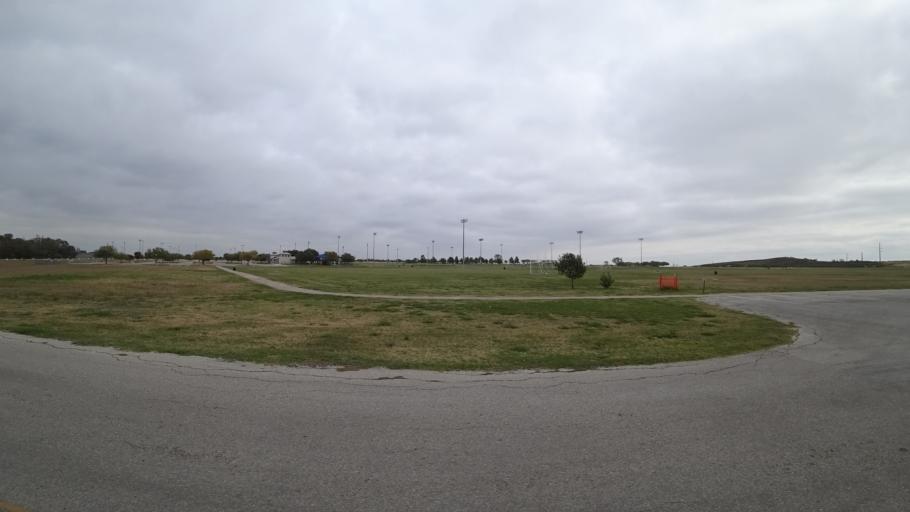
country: US
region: Texas
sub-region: Travis County
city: Pflugerville
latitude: 30.4100
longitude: -97.5986
